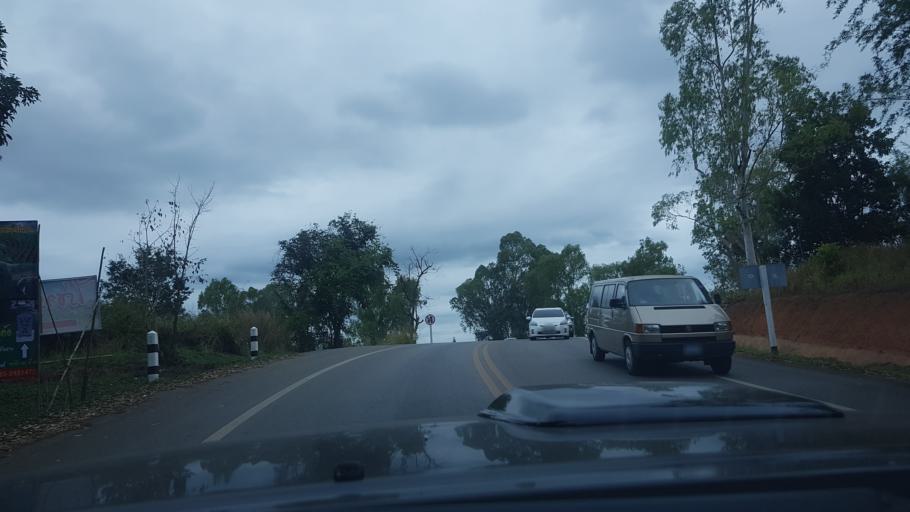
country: TH
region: Phetchabun
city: Khao Kho
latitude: 16.5620
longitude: 101.0105
